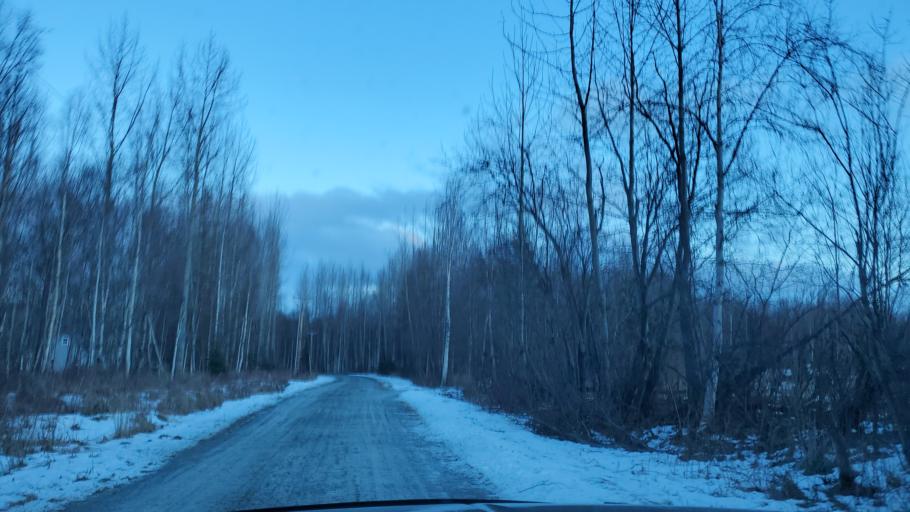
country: US
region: Alaska
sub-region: Matanuska-Susitna Borough
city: Lakes
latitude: 61.6655
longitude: -149.3360
